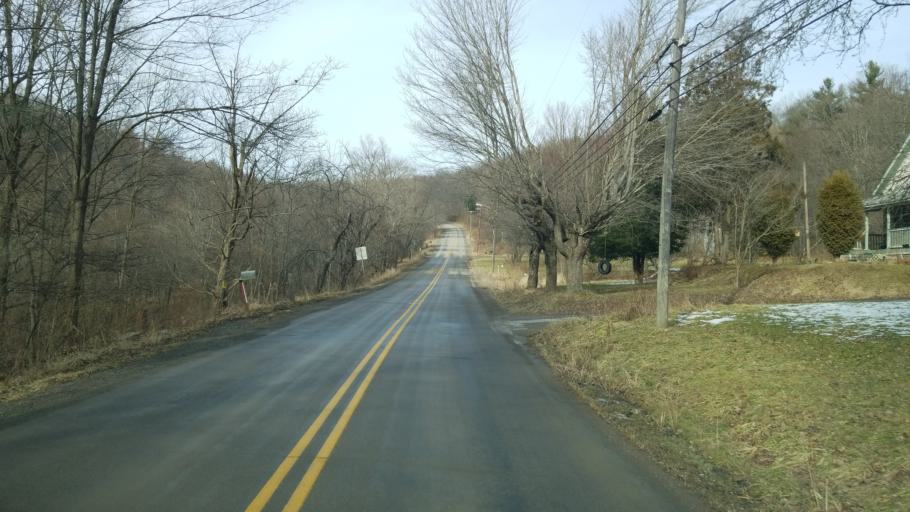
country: US
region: Pennsylvania
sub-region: Indiana County
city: Johnsonburg
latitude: 40.8275
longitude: -78.8355
